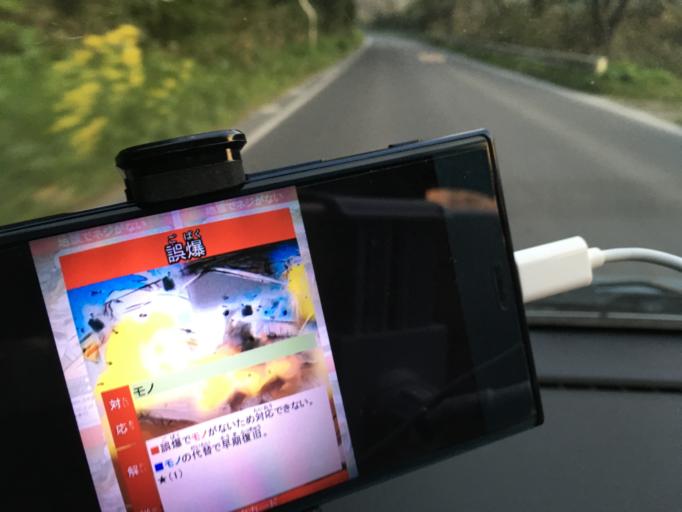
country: JP
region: Iwate
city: Ichinoseki
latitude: 38.9431
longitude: 141.2110
